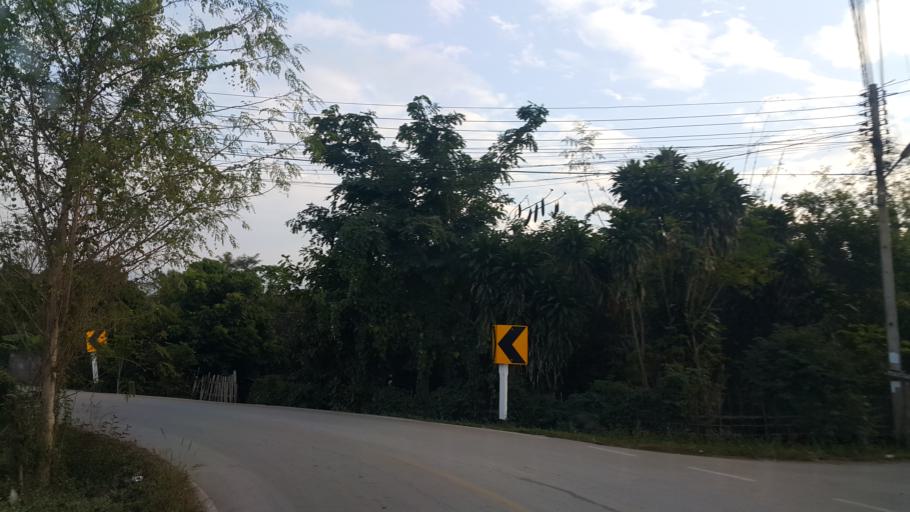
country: TH
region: Lampang
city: Sop Prap
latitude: 17.9017
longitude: 99.3287
